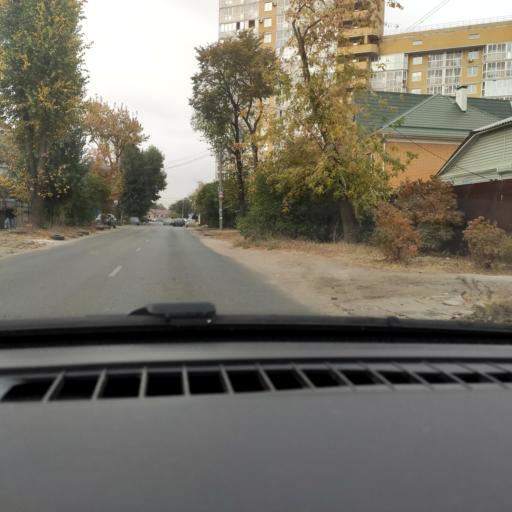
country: RU
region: Voronezj
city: Voronezh
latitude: 51.6998
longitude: 39.1983
